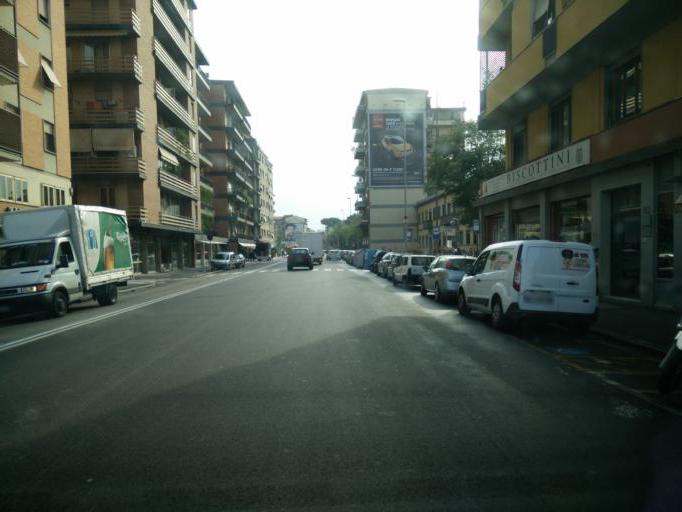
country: IT
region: Tuscany
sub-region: Province of Florence
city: Florence
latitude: 43.7923
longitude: 11.2157
